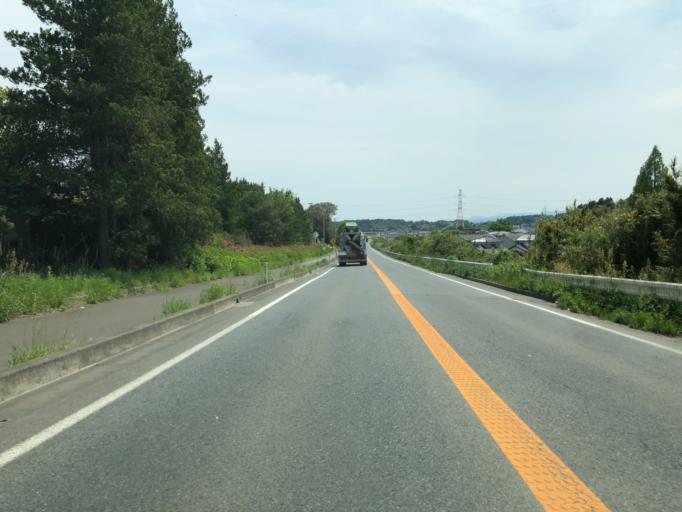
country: JP
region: Miyagi
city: Marumori
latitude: 37.8517
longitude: 140.9202
